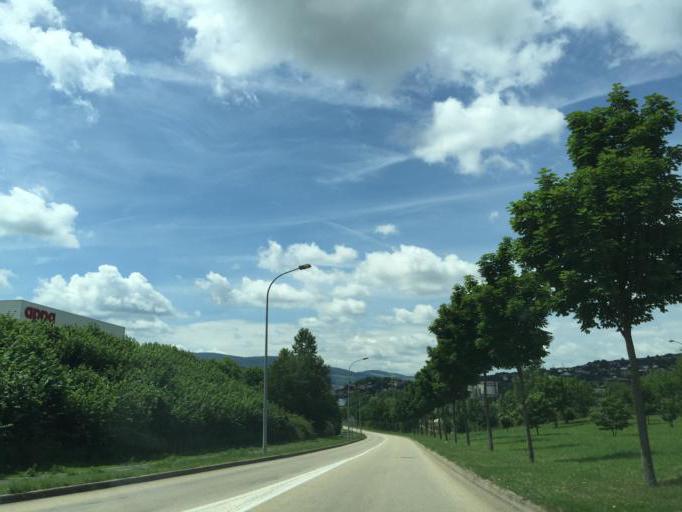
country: FR
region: Rhone-Alpes
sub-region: Departement de la Loire
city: Saint-Chamond
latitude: 45.4900
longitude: 4.5212
